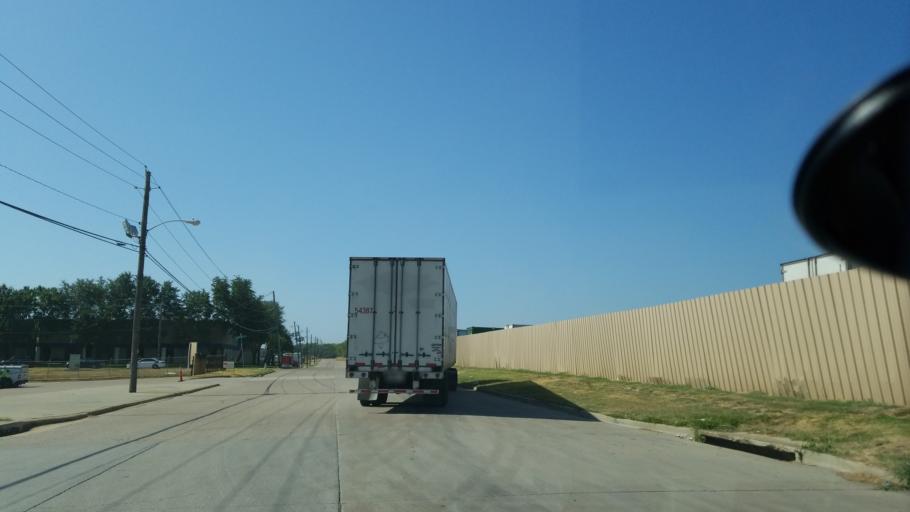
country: US
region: Texas
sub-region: Dallas County
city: Duncanville
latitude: 32.6965
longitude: -96.9161
